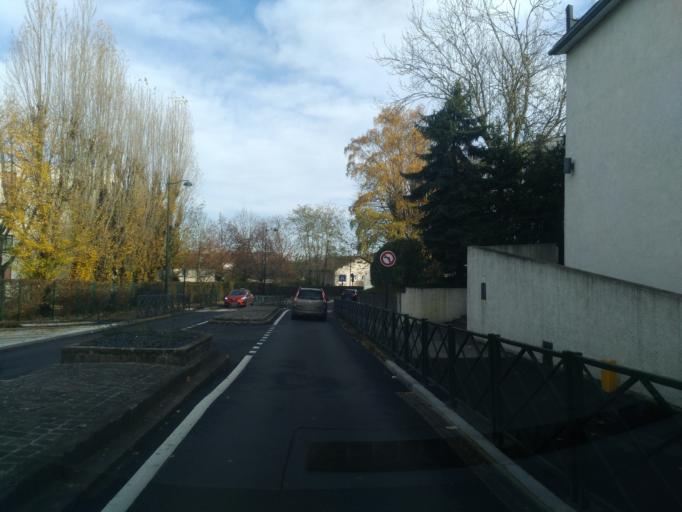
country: FR
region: Ile-de-France
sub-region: Departement des Yvelines
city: Les Clayes-sous-Bois
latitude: 48.8228
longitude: 1.9823
